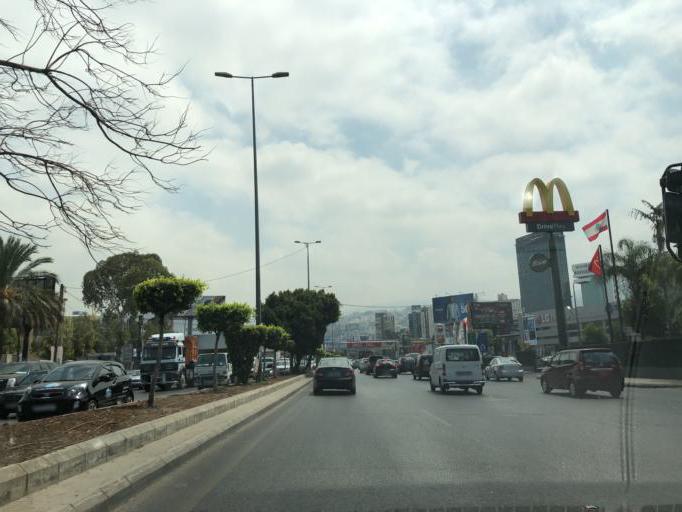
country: LB
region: Mont-Liban
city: Jdaidet el Matn
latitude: 33.8958
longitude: 35.5620
